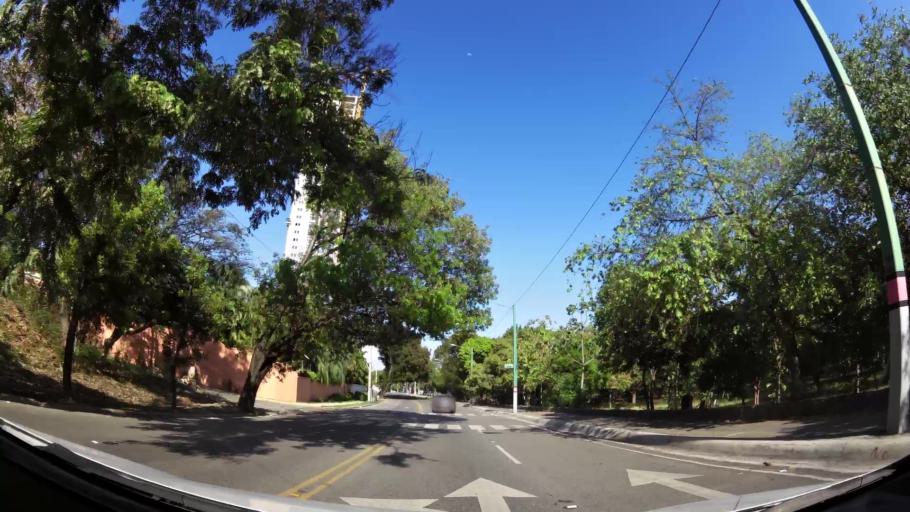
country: DO
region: Nacional
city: Bella Vista
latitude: 18.4374
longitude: -69.9727
